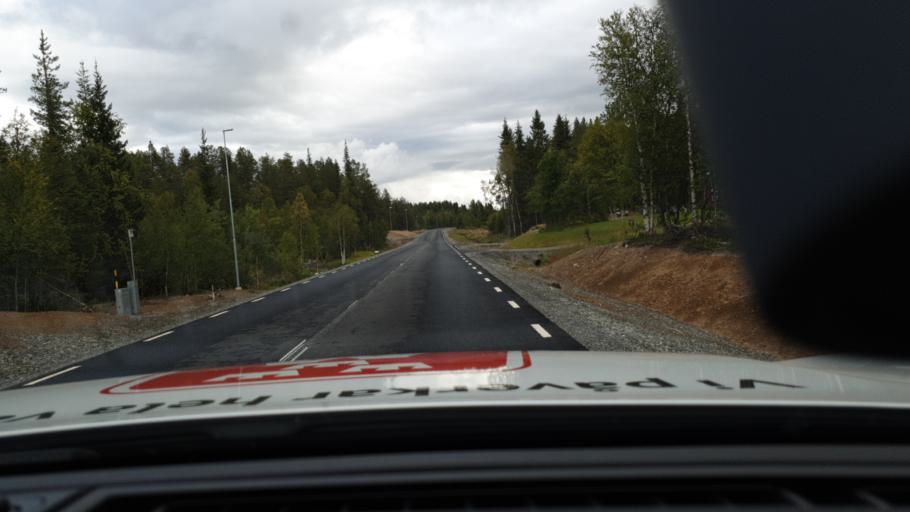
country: SE
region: Norrbotten
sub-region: Gallivare Kommun
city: Gaellivare
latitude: 66.8824
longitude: 21.2613
